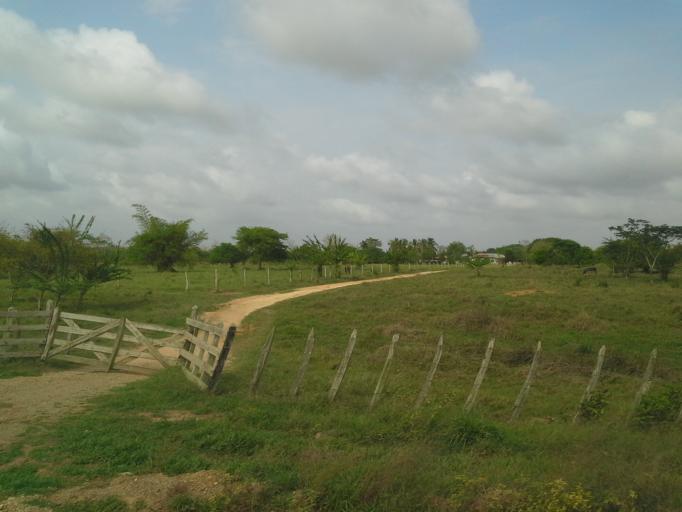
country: CO
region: Cordoba
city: Chima
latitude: 9.1412
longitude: -75.6142
